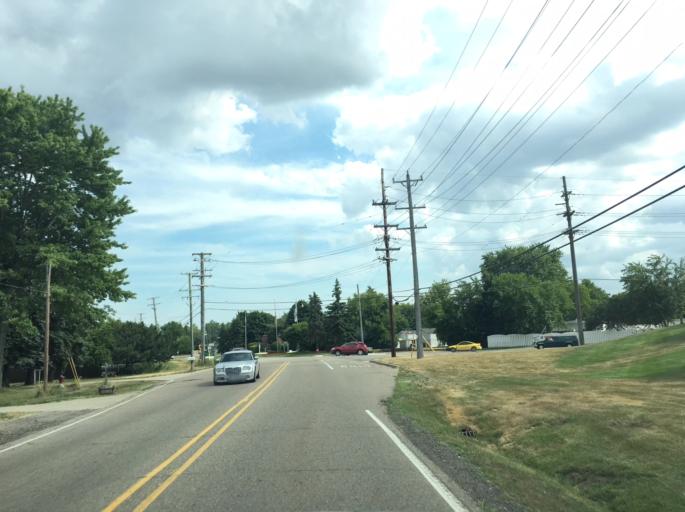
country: US
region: Michigan
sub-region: Macomb County
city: Utica
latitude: 42.6172
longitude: -83.0372
